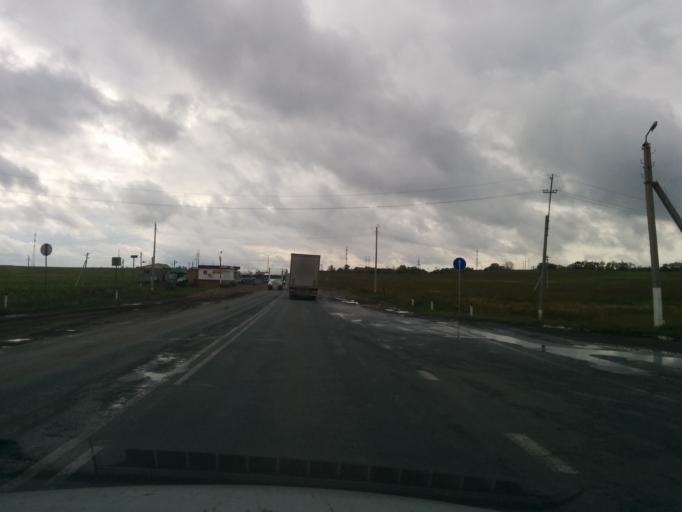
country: RU
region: Tatarstan
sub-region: Bavlinskiy Rayon
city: Bavly
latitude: 54.4206
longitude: 53.1542
